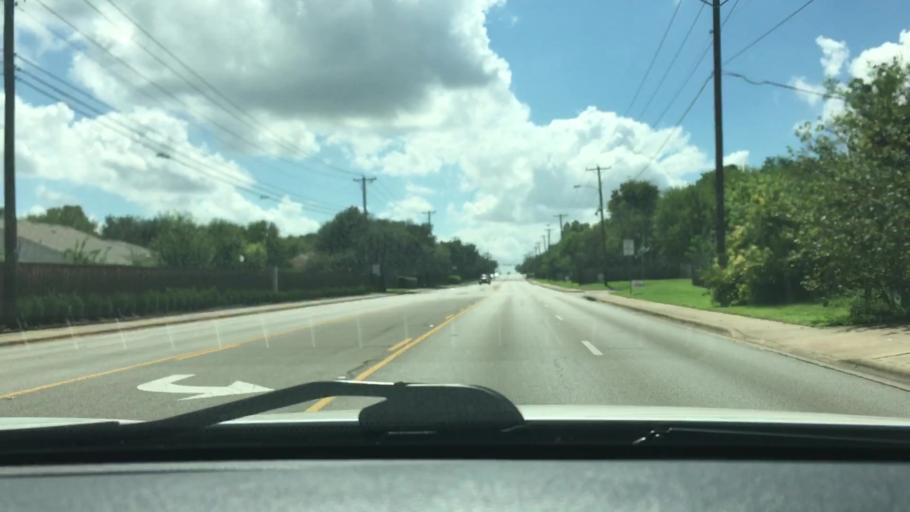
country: US
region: Texas
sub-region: Williamson County
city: Round Rock
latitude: 30.5355
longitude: -97.6681
